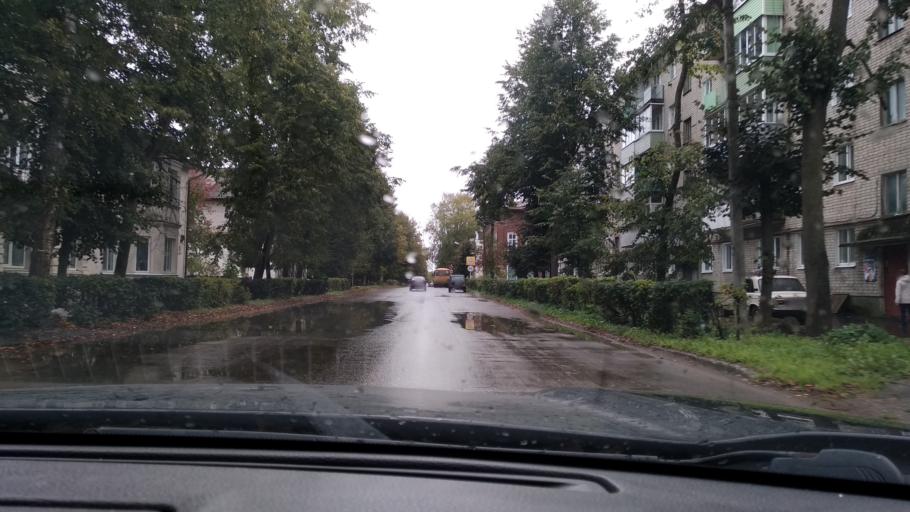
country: RU
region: Tverskaya
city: Kashin
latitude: 57.3562
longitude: 37.6013
